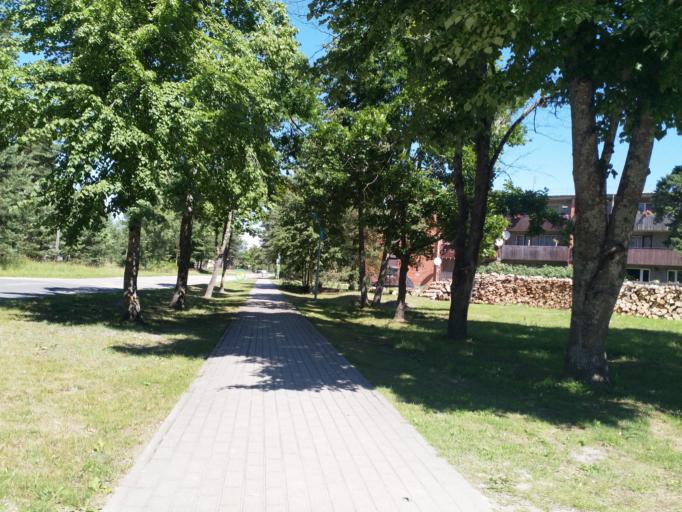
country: LV
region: Dundaga
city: Dundaga
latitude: 57.7357
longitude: 22.5812
